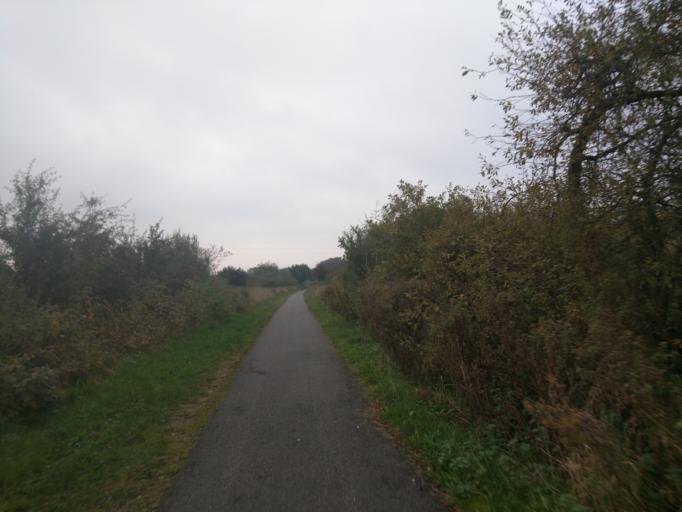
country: DK
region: Central Jutland
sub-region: Silkeborg Kommune
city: Silkeborg
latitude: 56.2251
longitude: 9.5083
